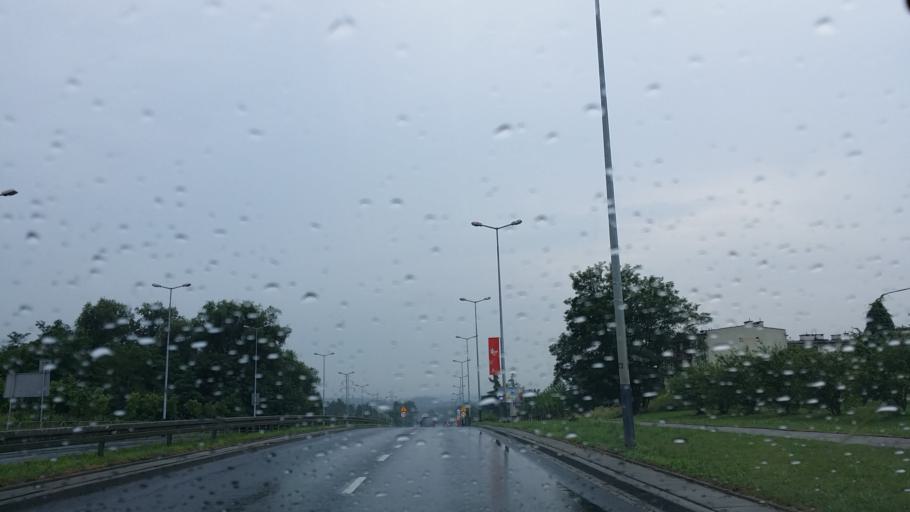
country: PL
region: Lesser Poland Voivodeship
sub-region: Krakow
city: Krakow
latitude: 50.0225
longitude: 19.9458
